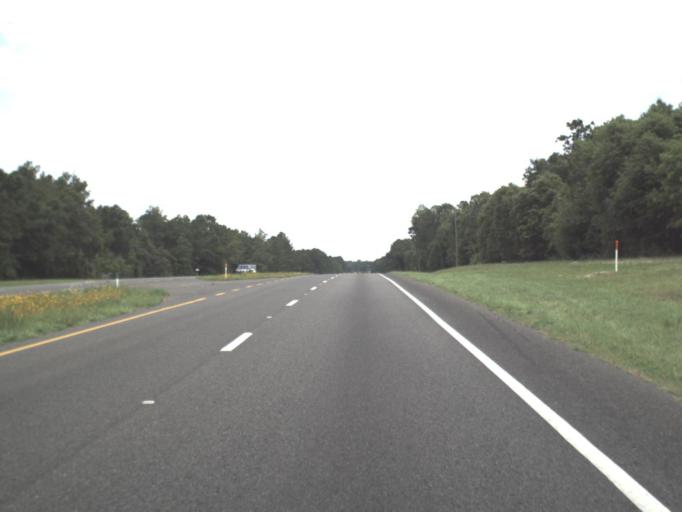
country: US
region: Florida
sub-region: Nassau County
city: Hilliard
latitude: 30.7549
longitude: -81.9622
